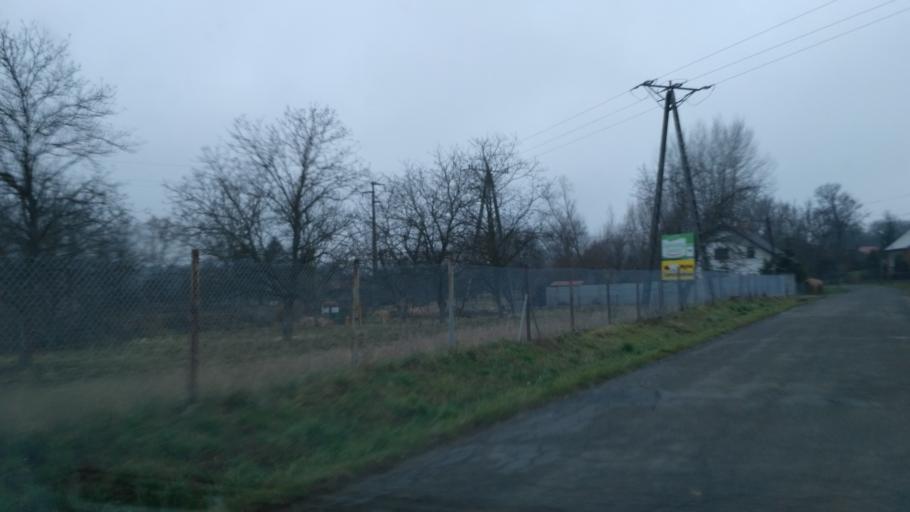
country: PL
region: Subcarpathian Voivodeship
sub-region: Powiat przeworski
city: Mirocin
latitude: 50.0435
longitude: 22.5552
